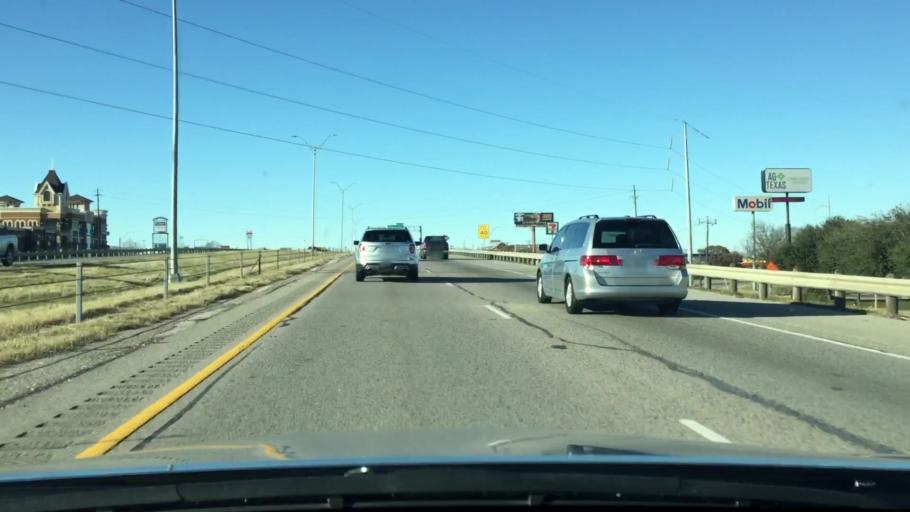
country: US
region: Texas
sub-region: Johnson County
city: Burleson
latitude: 32.5419
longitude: -97.3139
